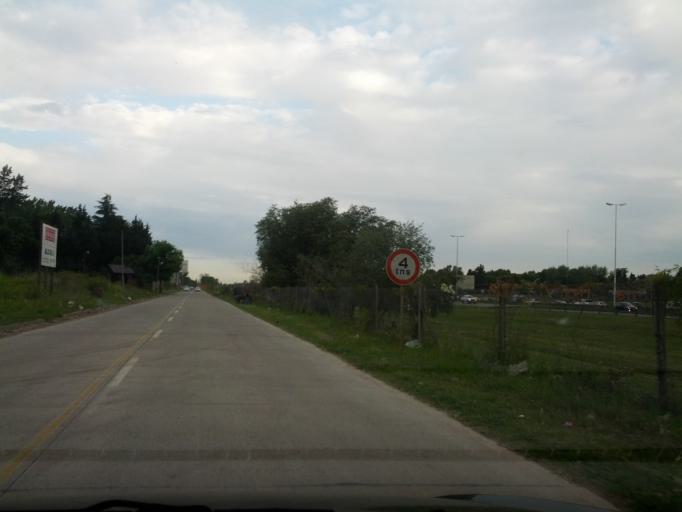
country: AR
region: Buenos Aires
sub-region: Partido de General Rodriguez
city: General Rodriguez
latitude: -34.6134
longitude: -58.8567
